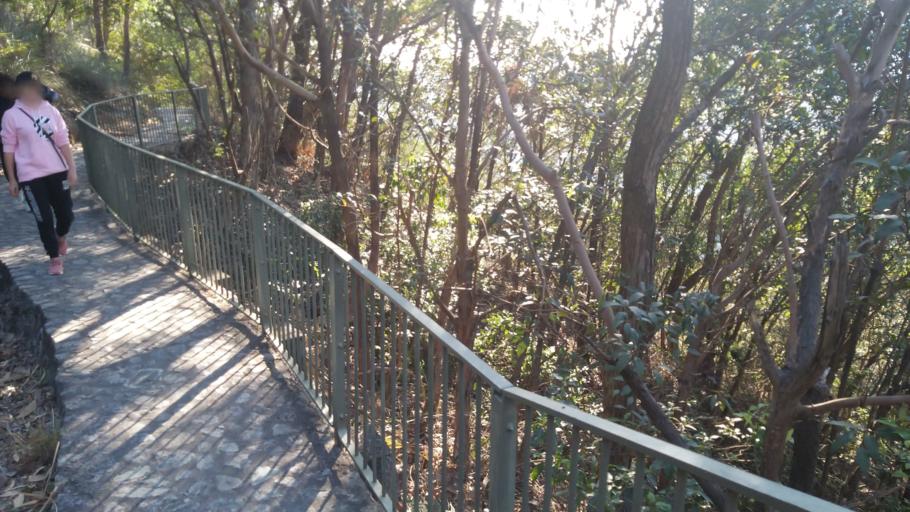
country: HK
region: Tuen Mun
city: Tuen Mun
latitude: 22.3967
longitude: 113.9833
